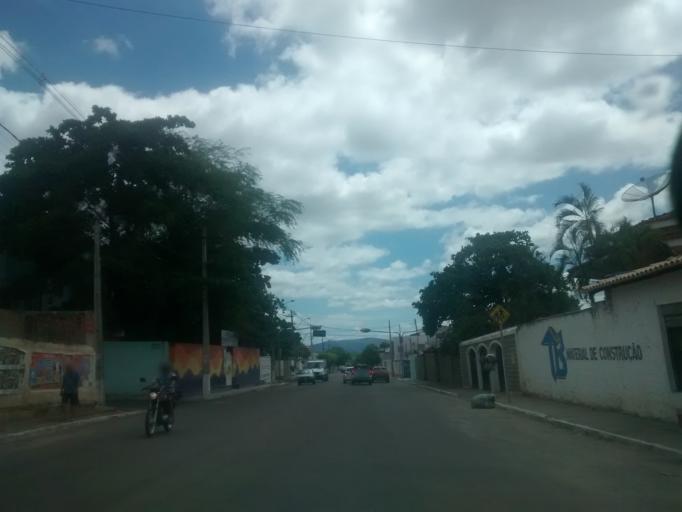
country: BR
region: Bahia
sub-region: Brumado
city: Brumado
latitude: -14.2064
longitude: -41.6740
